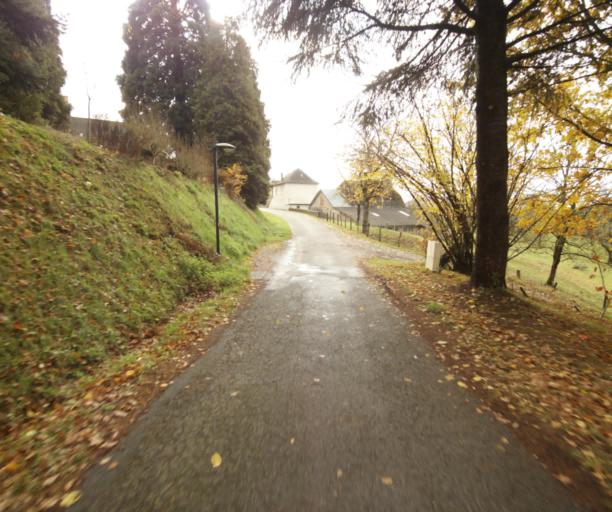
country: FR
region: Limousin
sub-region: Departement de la Correze
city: Cornil
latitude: 45.2137
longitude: 1.6370
